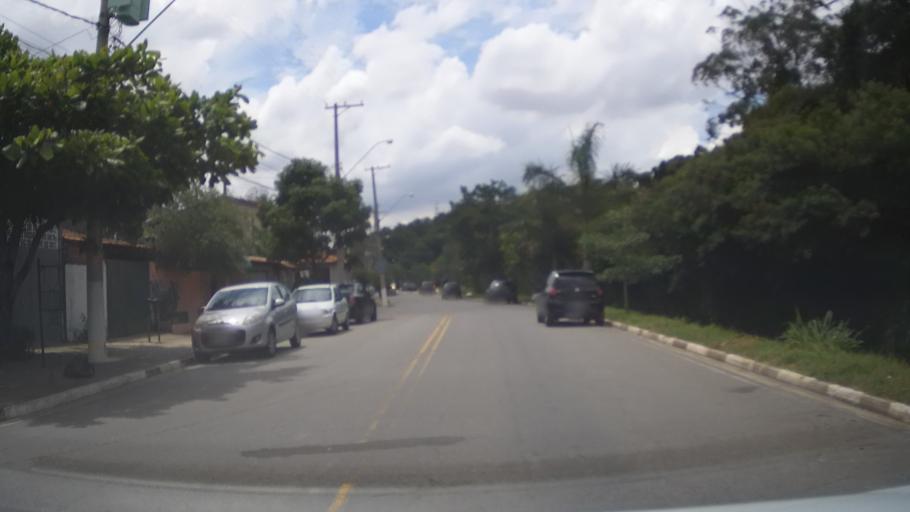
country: BR
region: Sao Paulo
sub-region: Vinhedo
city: Vinhedo
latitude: -23.0089
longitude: -46.9830
